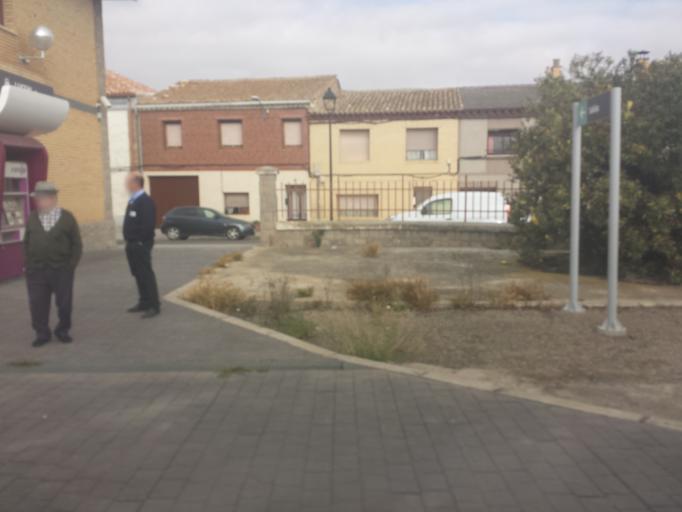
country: ES
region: Aragon
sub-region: Provincia de Zaragoza
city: Luceni
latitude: 41.8261
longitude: -1.2437
